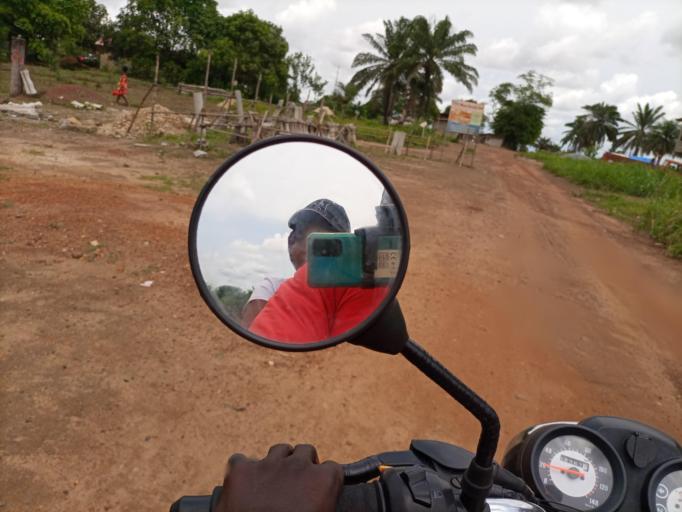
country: SL
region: Southern Province
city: Baoma
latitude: 7.9731
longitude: -11.7150
